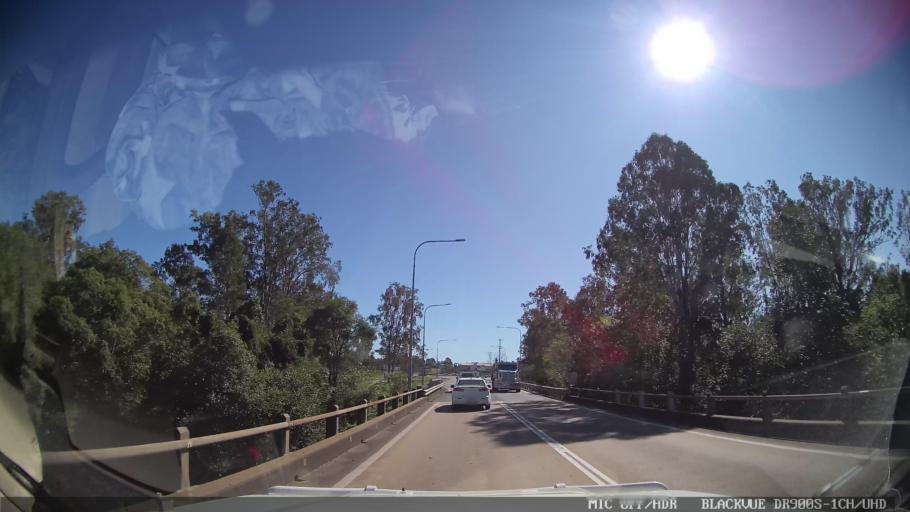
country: AU
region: Queensland
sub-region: Gympie Regional Council
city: Monkland
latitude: -26.2327
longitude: 152.6979
